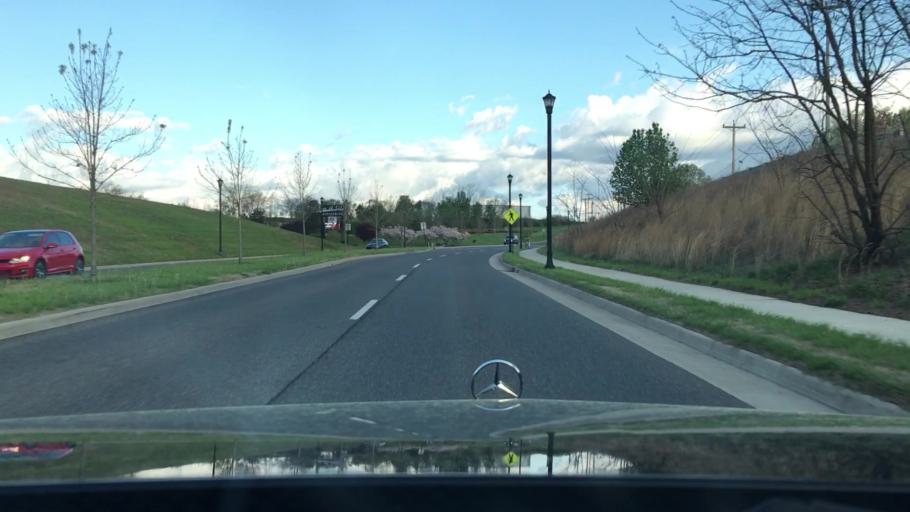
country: US
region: Virginia
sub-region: Campbell County
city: Timberlake
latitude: 37.3418
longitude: -79.2307
